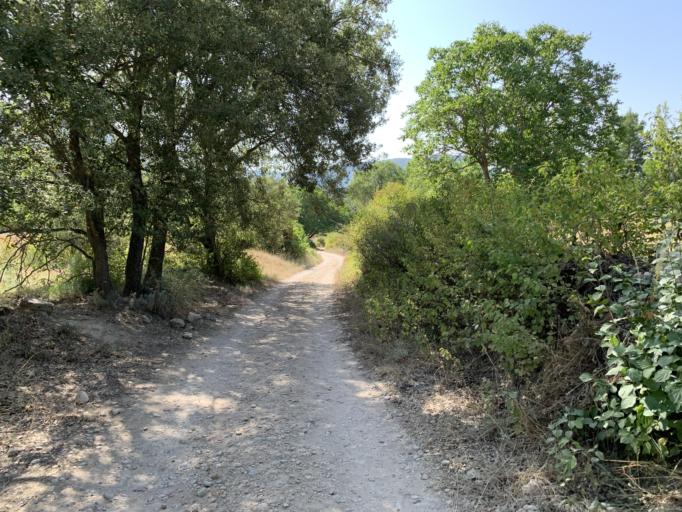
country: ES
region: Castille-La Mancha
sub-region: Provincia de Guadalajara
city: Ocentejo
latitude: 40.7655
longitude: -2.3945
